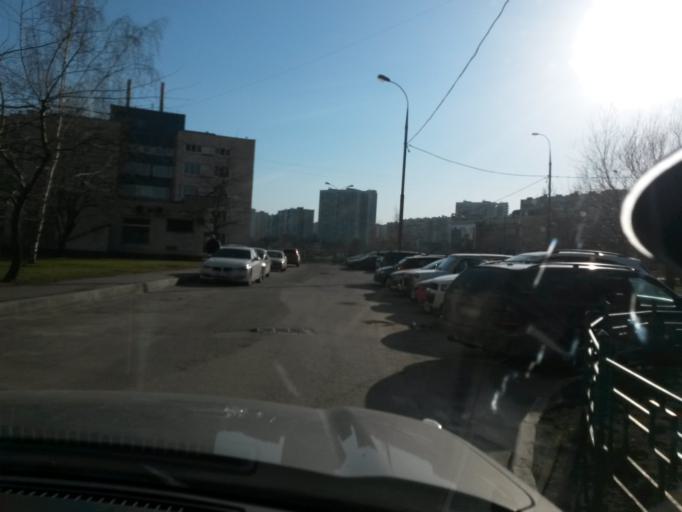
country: RU
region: Moscow
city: Annino
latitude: 55.5754
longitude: 37.5829
